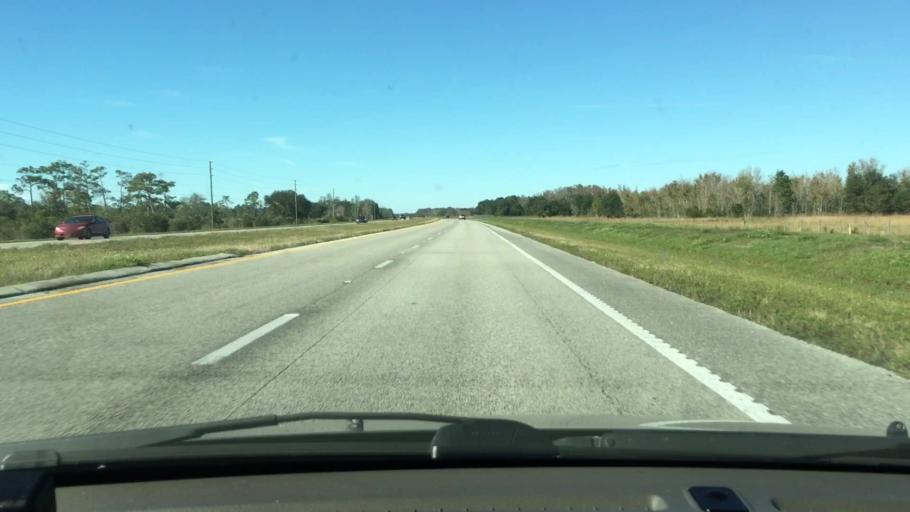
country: US
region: Florida
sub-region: Brevard County
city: June Park
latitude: 28.1272
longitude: -80.9795
